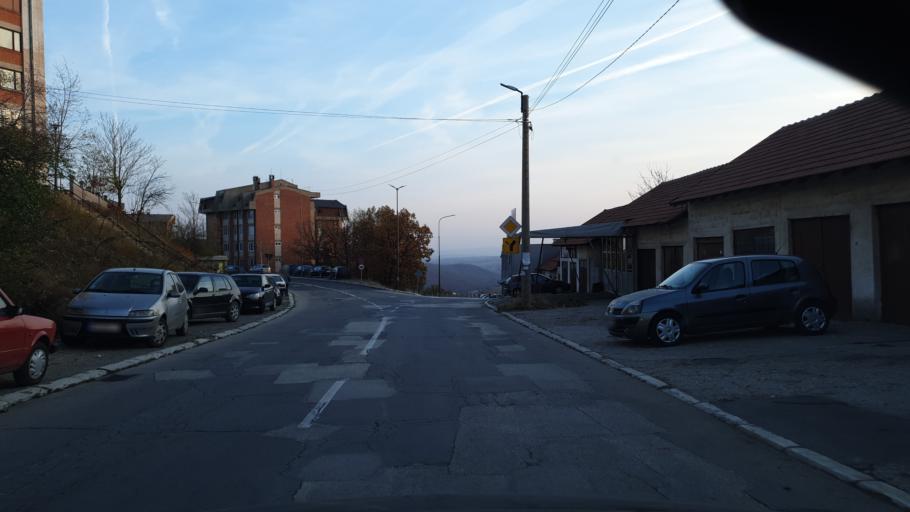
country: RS
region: Central Serbia
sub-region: Borski Okrug
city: Bor
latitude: 44.0561
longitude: 22.0954
